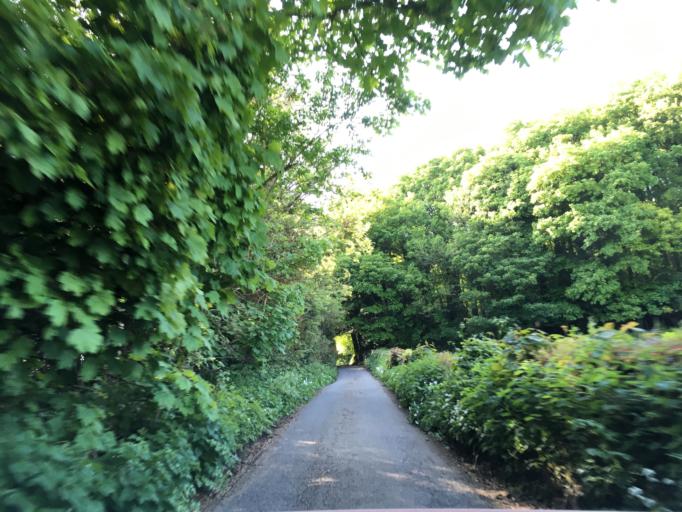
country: GB
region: England
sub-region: Gloucestershire
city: Nailsworth
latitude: 51.6643
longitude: -2.2596
